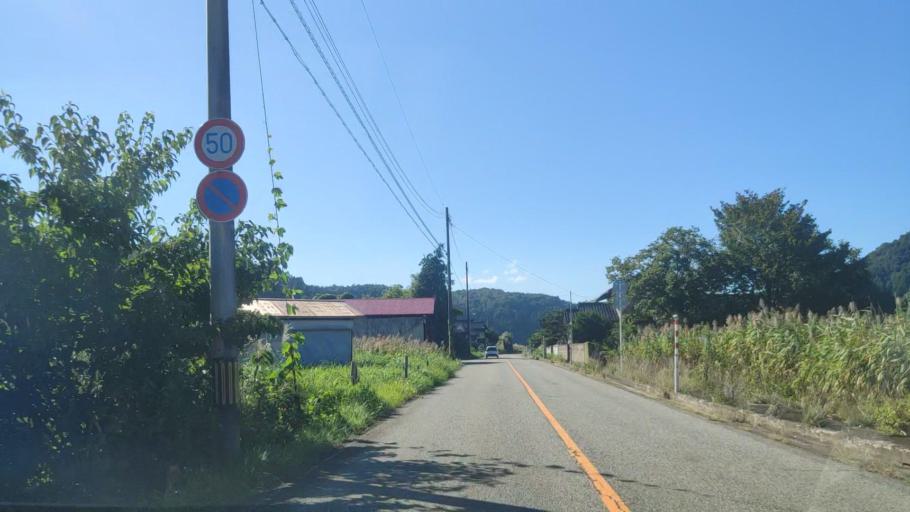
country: JP
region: Ishikawa
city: Nanao
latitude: 37.2564
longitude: 137.0798
